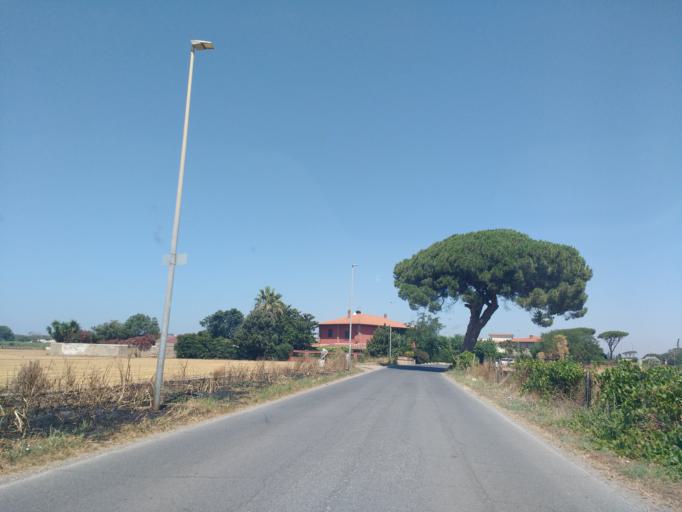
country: IT
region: Latium
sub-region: Citta metropolitana di Roma Capitale
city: Fregene
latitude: 41.8501
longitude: 12.2186
